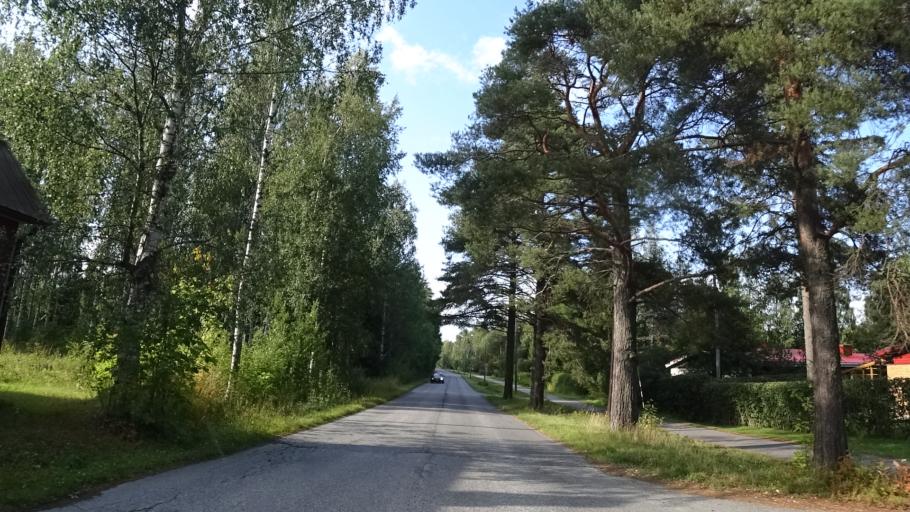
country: FI
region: North Karelia
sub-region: Pielisen Karjala
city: Lieksa
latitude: 63.3327
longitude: 30.0298
